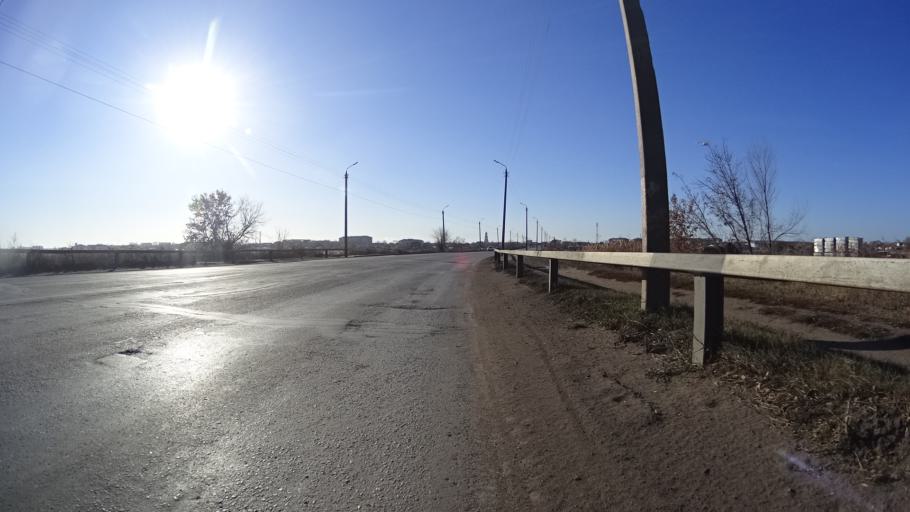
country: RU
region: Chelyabinsk
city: Troitsk
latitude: 54.0936
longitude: 61.5787
